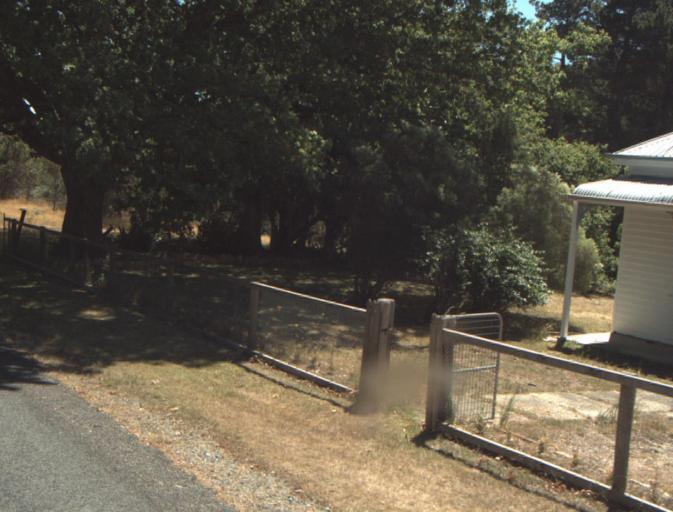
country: AU
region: Tasmania
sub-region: Dorset
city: Scottsdale
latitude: -41.2956
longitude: 147.3526
